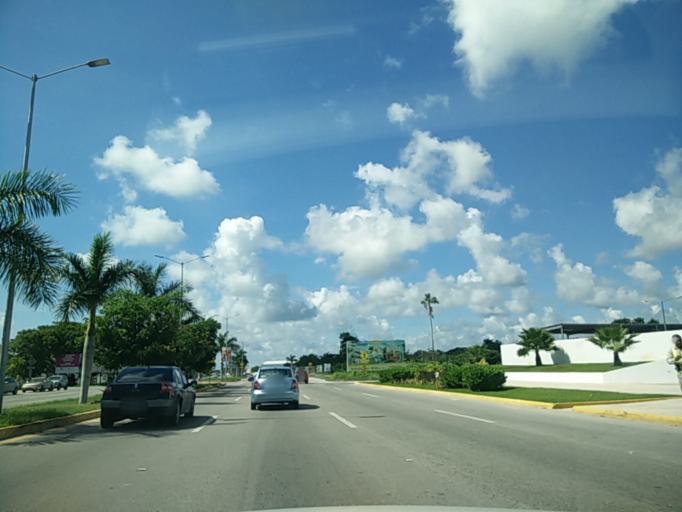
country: MX
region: Quintana Roo
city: Playa del Carmen
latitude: 20.6666
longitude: -87.0690
